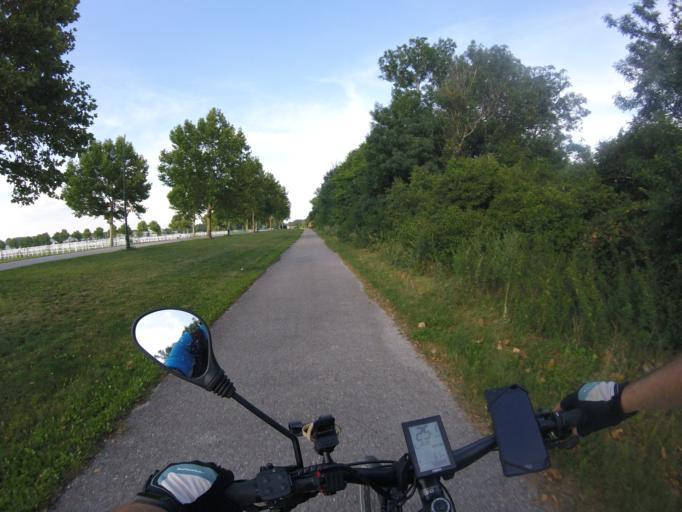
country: AT
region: Lower Austria
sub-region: Politischer Bezirk Baden
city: Ebreichsdorf
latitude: 47.9666
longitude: 16.3767
